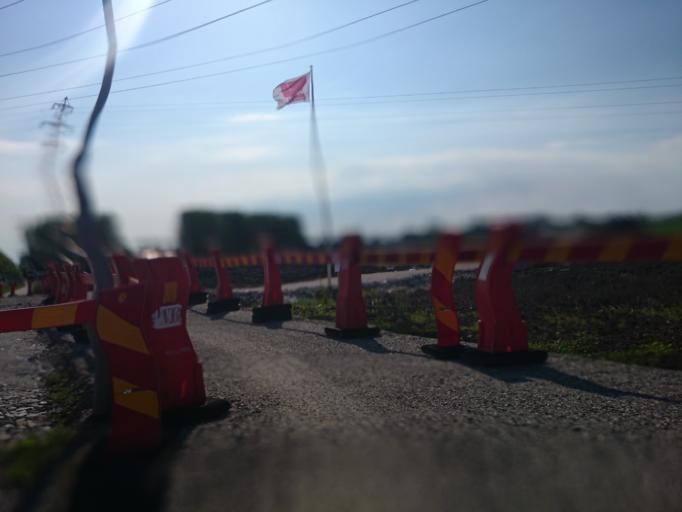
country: SE
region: Skane
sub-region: Staffanstorps Kommun
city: Hjaerup
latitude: 55.6689
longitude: 13.1592
